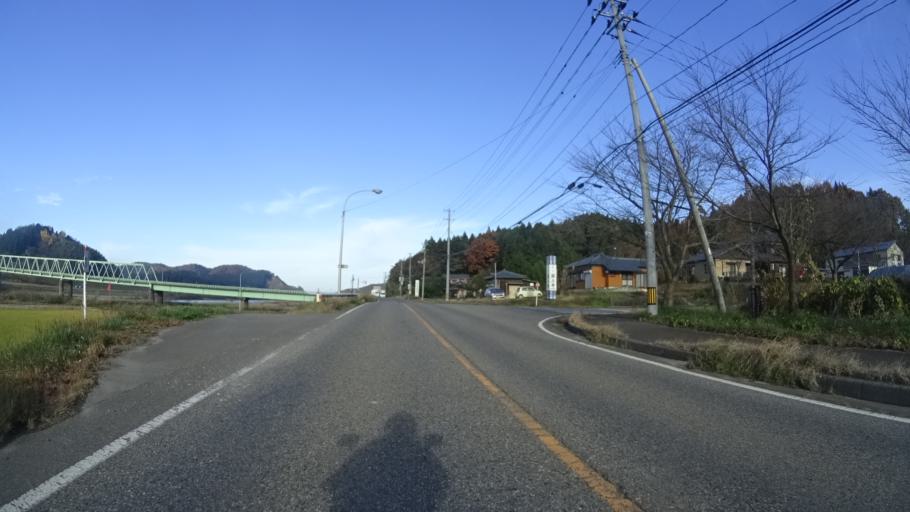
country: JP
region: Niigata
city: Yoshida-kasugacho
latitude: 37.6524
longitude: 138.8099
